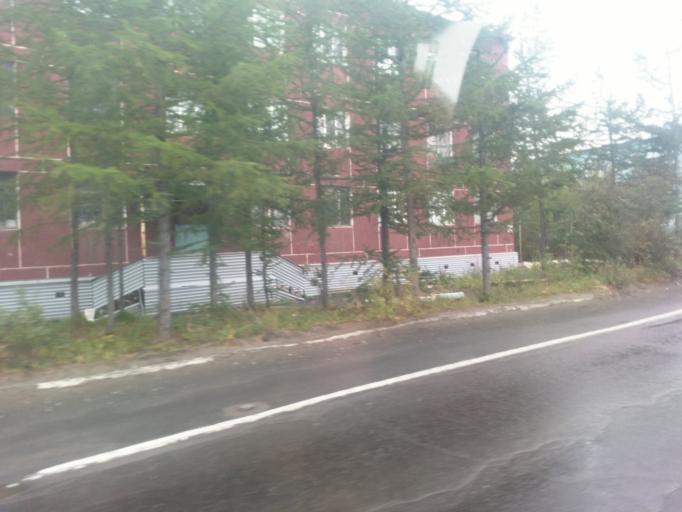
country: RU
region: Krasnoyarskiy
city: Dudinka
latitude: 69.4041
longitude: 86.2148
